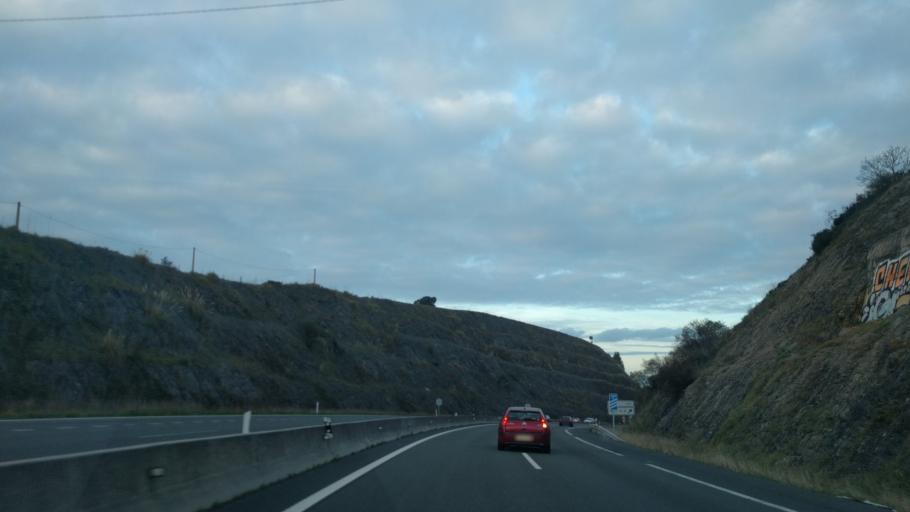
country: ES
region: Cantabria
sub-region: Provincia de Cantabria
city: Castro-Urdiales
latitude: 43.3583
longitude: -3.2185
